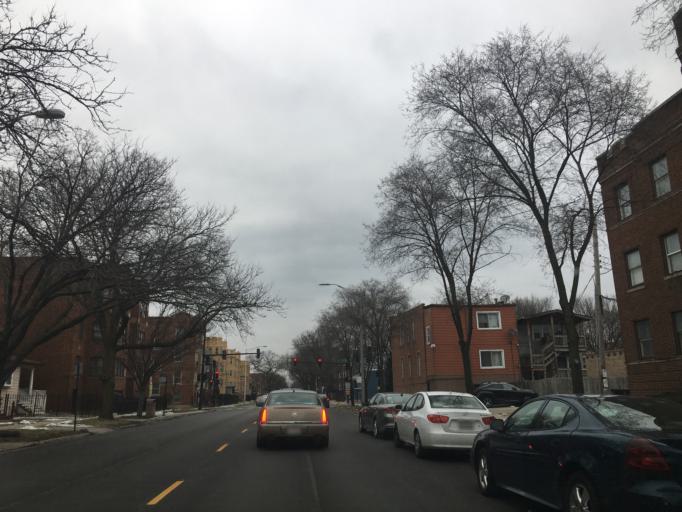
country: US
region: Illinois
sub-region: Cook County
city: Oak Park
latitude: 41.8976
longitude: -87.7752
